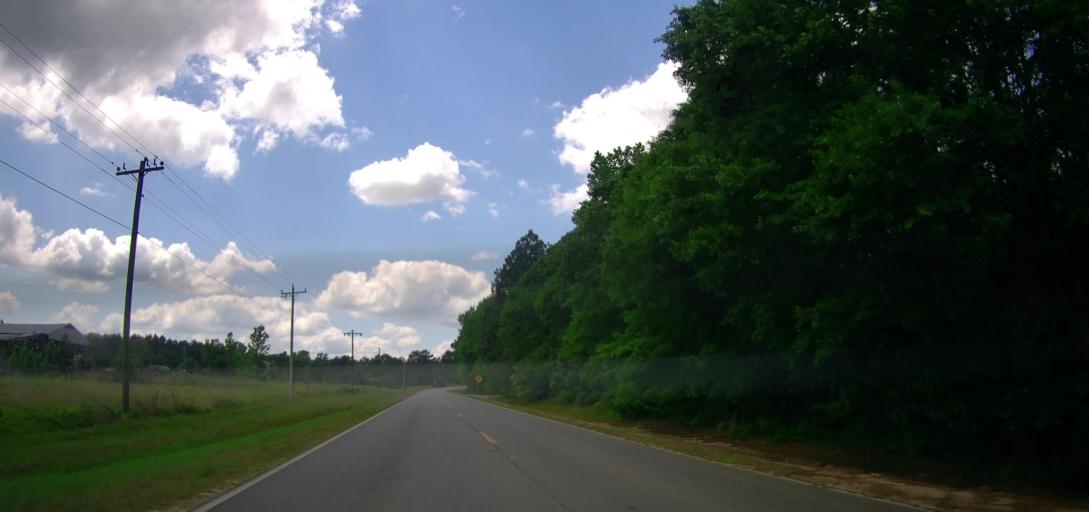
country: US
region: Georgia
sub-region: Laurens County
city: East Dublin
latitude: 32.5193
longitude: -82.7780
